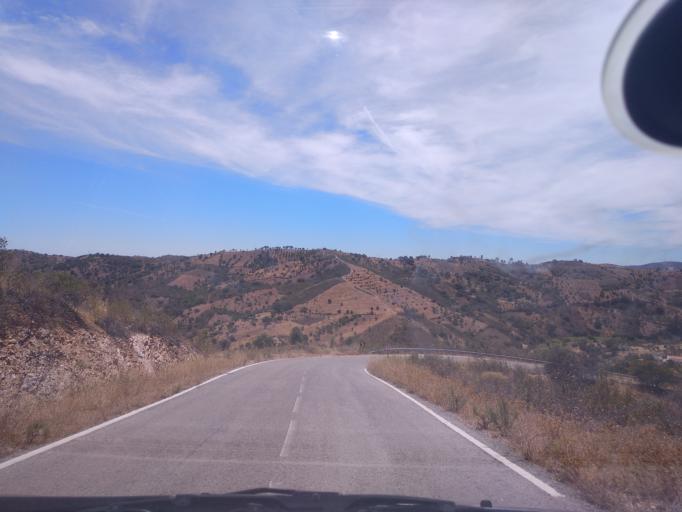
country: PT
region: Faro
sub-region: Sao Bras de Alportel
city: Sao Bras de Alportel
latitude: 37.1847
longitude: -7.7973
